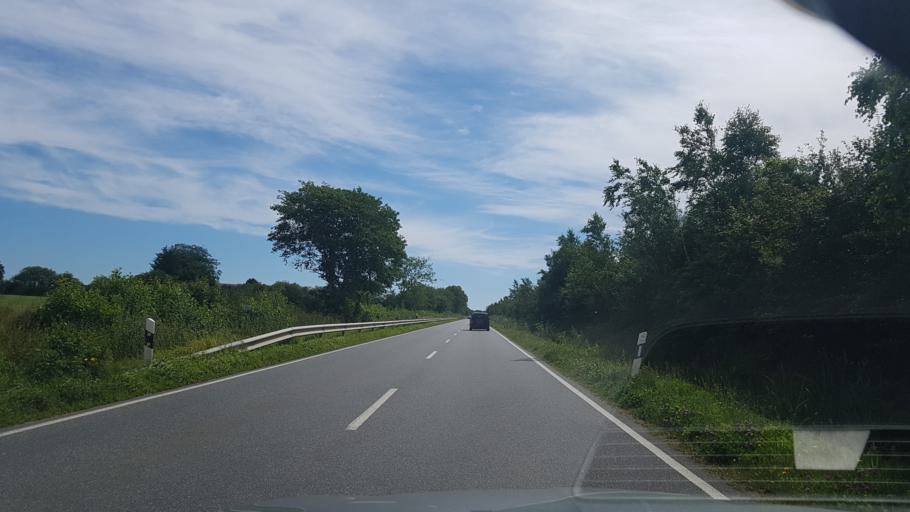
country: DE
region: Schleswig-Holstein
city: Osterby
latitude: 54.8029
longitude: 9.2493
